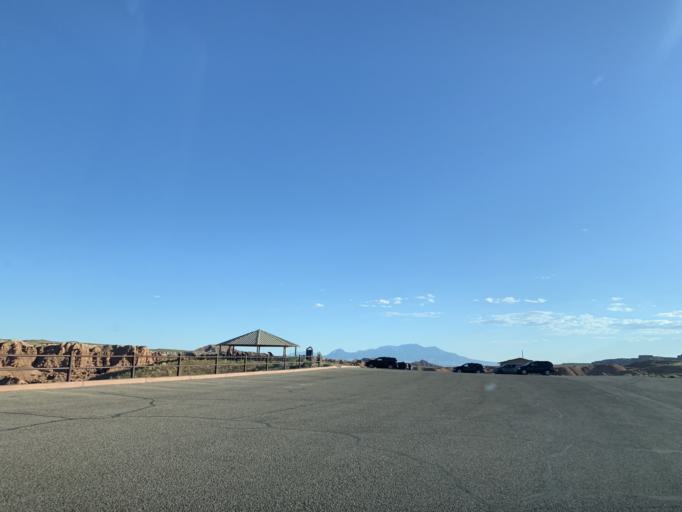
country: US
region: Utah
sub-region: Emery County
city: Ferron
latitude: 38.5650
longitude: -110.7033
